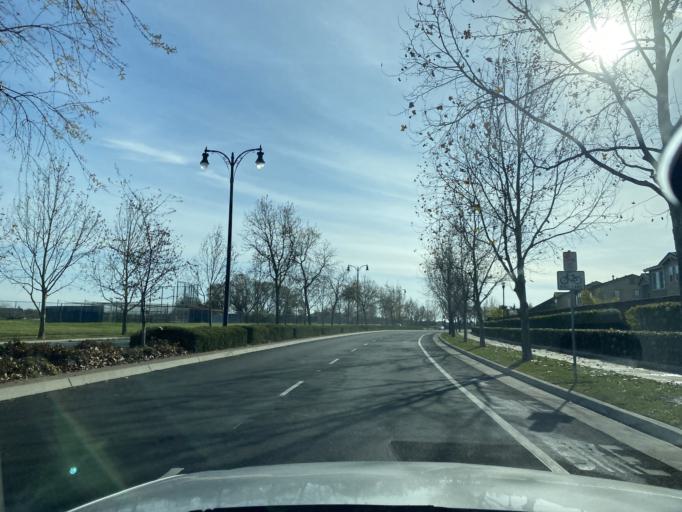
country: US
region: California
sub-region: Sacramento County
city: Elk Grove
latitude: 38.3996
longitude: -121.4009
